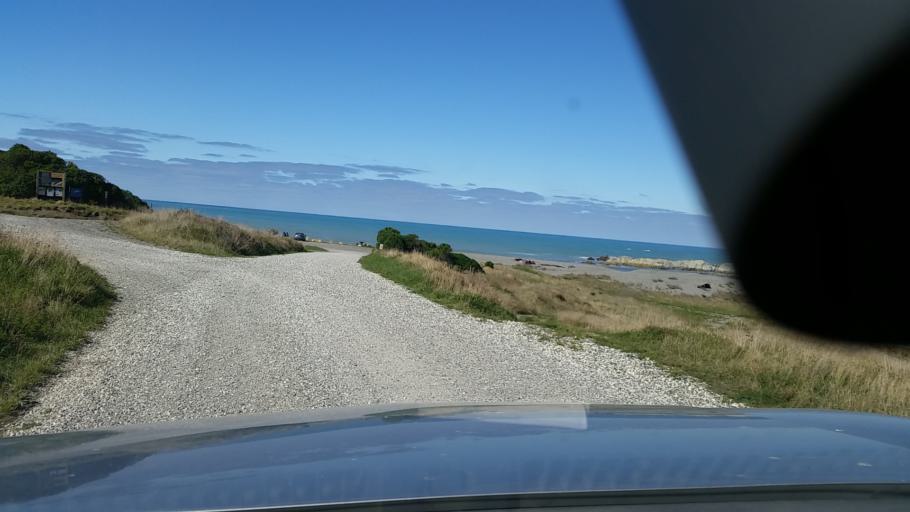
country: NZ
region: Marlborough
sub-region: Marlborough District
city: Blenheim
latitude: -41.8439
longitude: 174.1823
